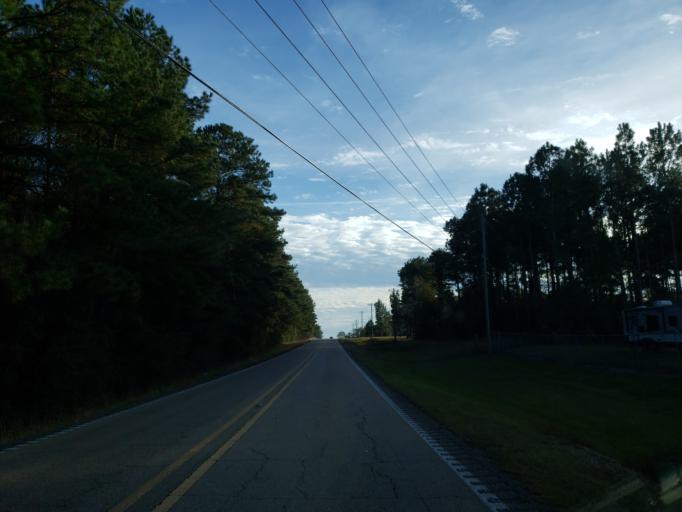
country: US
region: Mississippi
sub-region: Lamar County
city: West Hattiesburg
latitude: 31.2755
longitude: -89.4659
